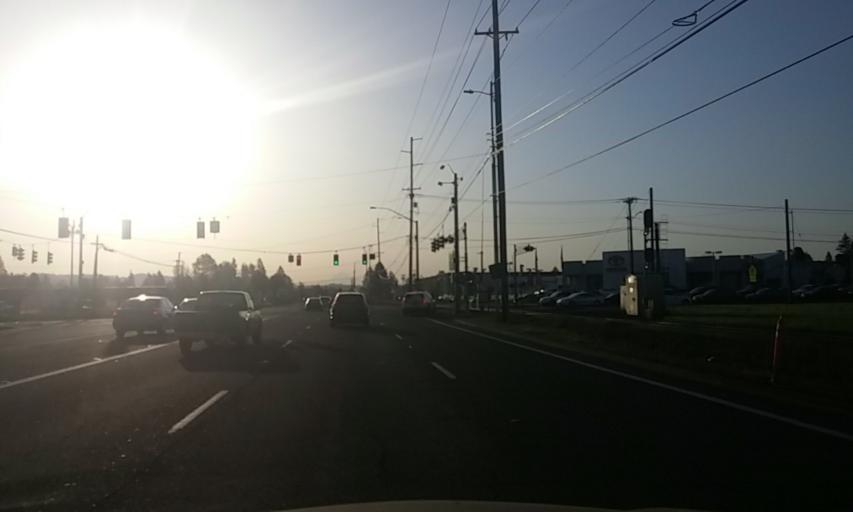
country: US
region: Oregon
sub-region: Washington County
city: Beaverton
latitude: 45.4896
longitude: -122.8269
